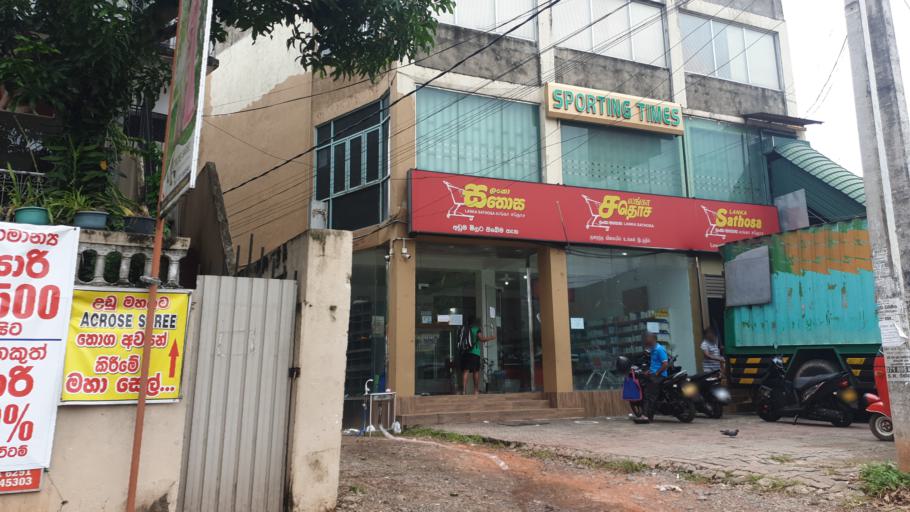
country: LK
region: Western
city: Gampaha
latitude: 7.0943
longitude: 79.9936
